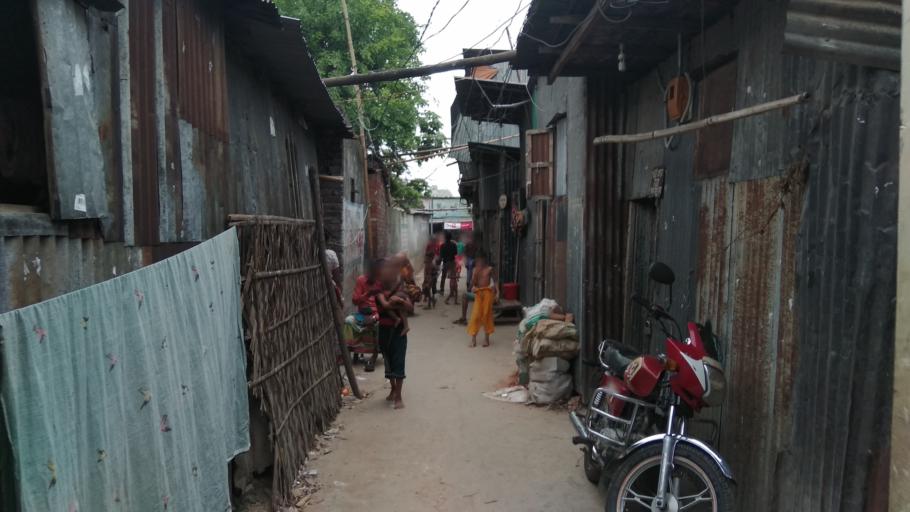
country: BD
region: Dhaka
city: Tungi
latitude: 23.8214
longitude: 90.3809
